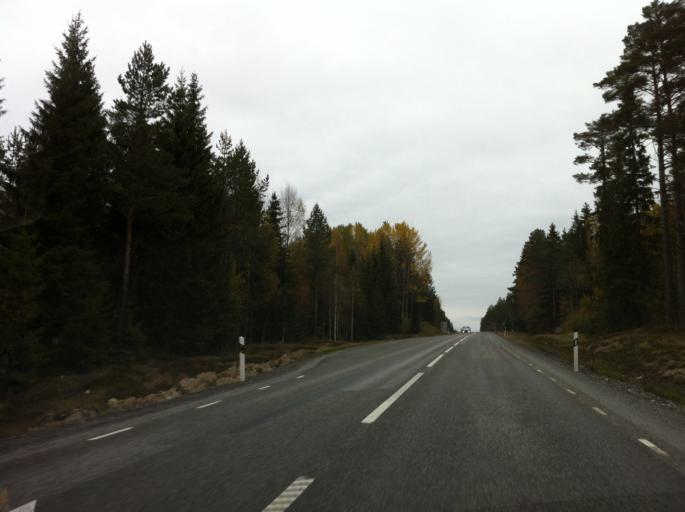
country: SE
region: OErebro
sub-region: Ljusnarsbergs Kommun
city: Kopparberg
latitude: 59.9223
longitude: 15.0215
